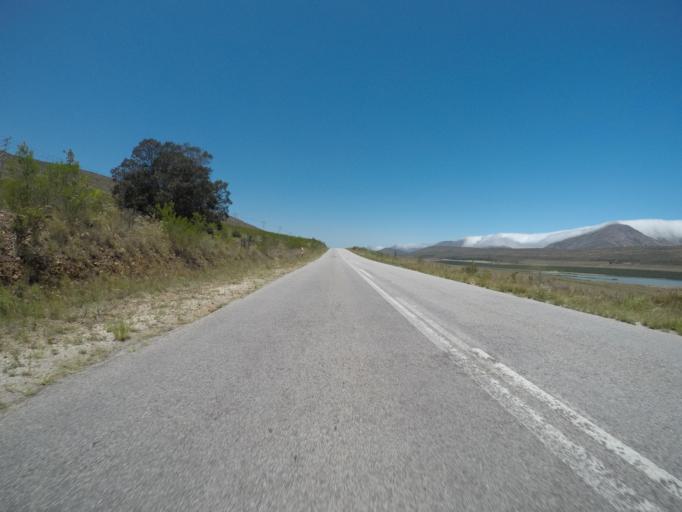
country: ZA
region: Eastern Cape
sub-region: Cacadu District Municipality
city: Kareedouw
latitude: -33.8343
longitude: 23.9108
